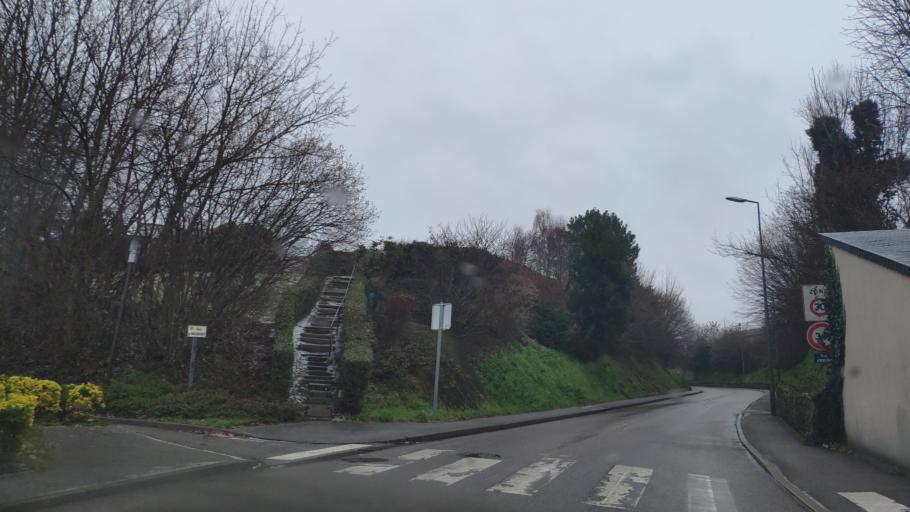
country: FR
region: Haute-Normandie
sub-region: Departement de la Seine-Maritime
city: Cany-Barville
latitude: 49.7890
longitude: 0.6392
